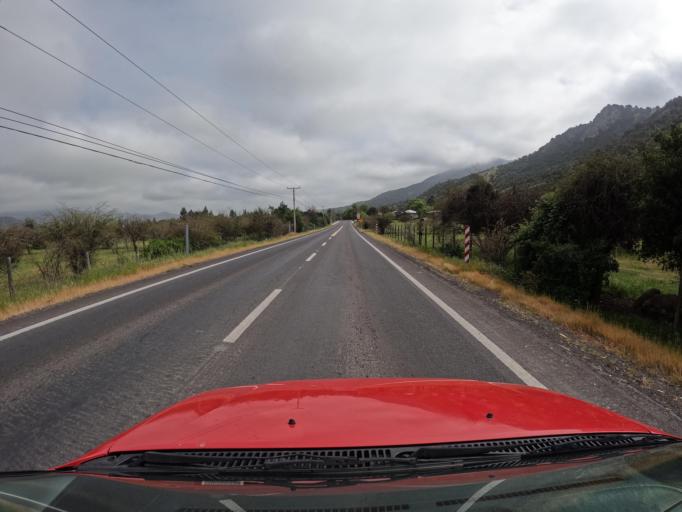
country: CL
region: Maule
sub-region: Provincia de Curico
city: Teno
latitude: -34.8146
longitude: -71.2125
